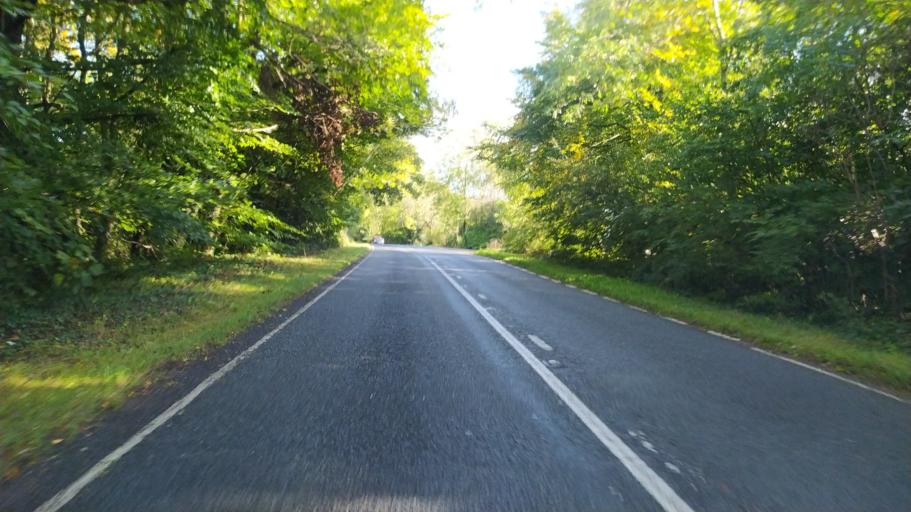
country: GB
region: England
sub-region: Hampshire
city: Lyndhurst
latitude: 50.8653
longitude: -1.5948
